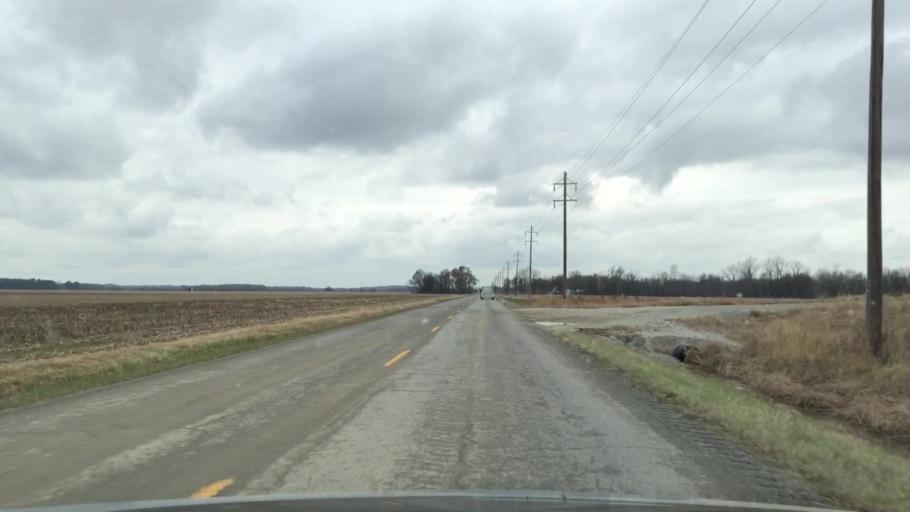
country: US
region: Kentucky
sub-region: McLean County
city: Calhoun
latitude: 37.5243
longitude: -87.2917
